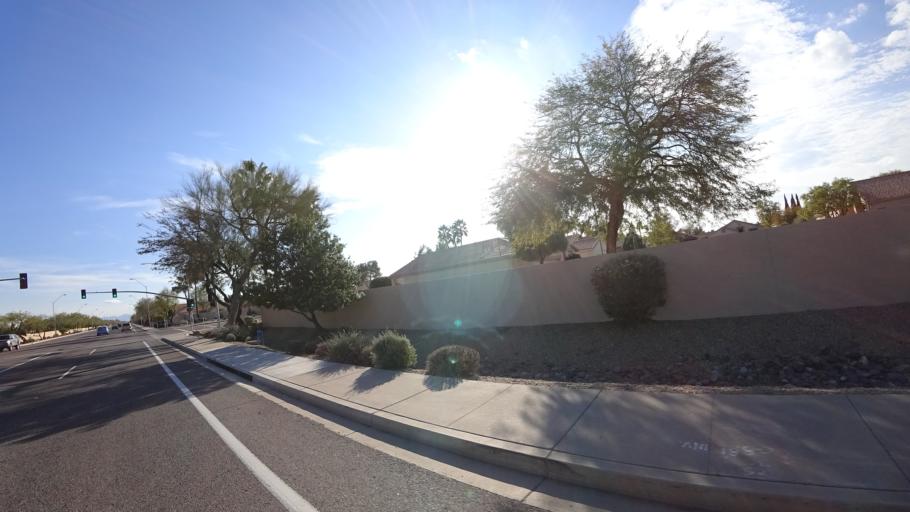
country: US
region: Arizona
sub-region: Maricopa County
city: Sun City
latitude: 33.6642
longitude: -112.2551
